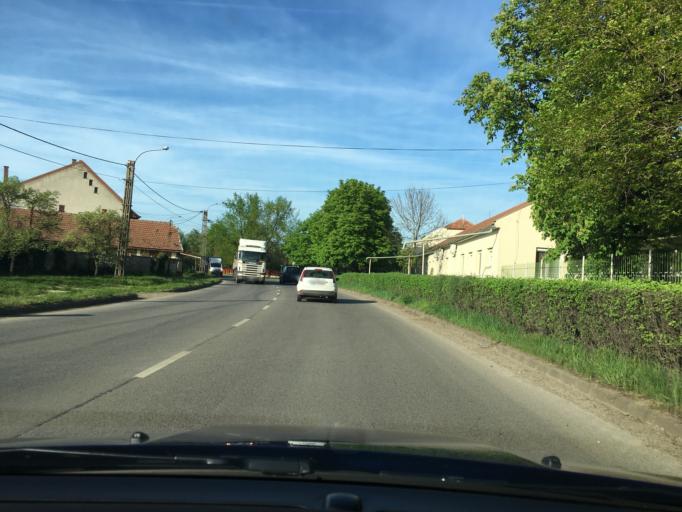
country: HU
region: Bekes
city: Korosladany
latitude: 46.9640
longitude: 21.0870
